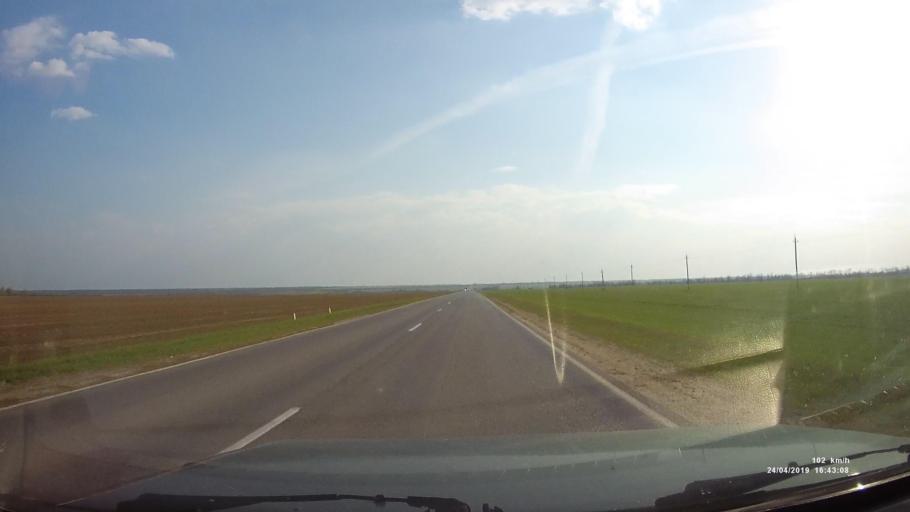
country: RU
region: Rostov
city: Gundorovskiy
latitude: 46.7982
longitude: 41.8445
